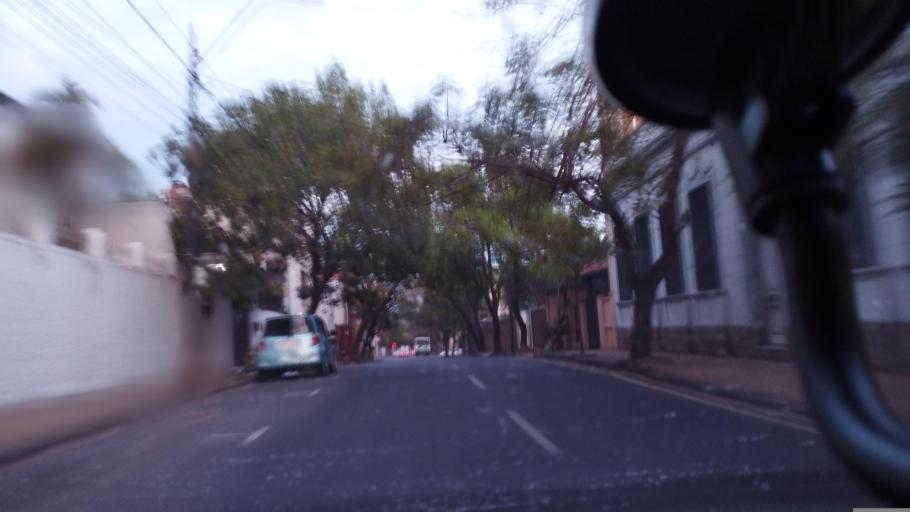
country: PY
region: Asuncion
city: Asuncion
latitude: -25.2893
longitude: -57.6222
